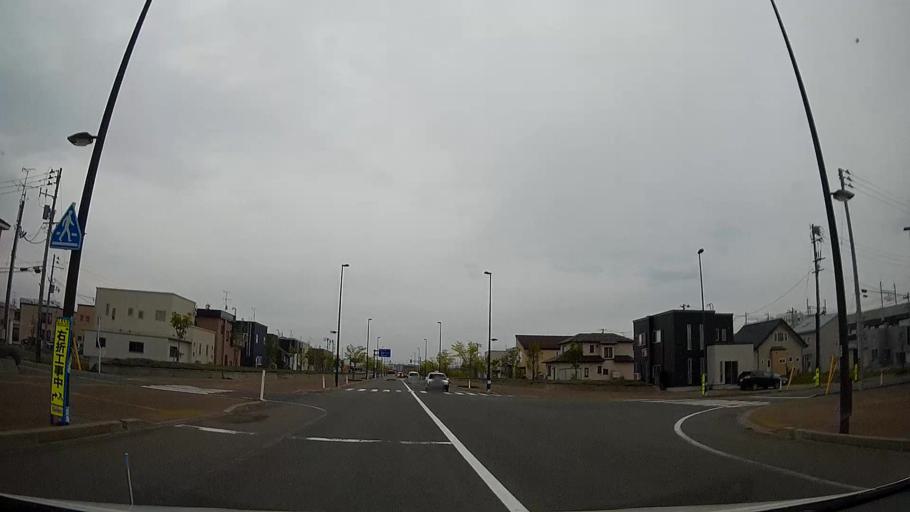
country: JP
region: Aomori
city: Aomori Shi
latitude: 40.8323
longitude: 140.6953
